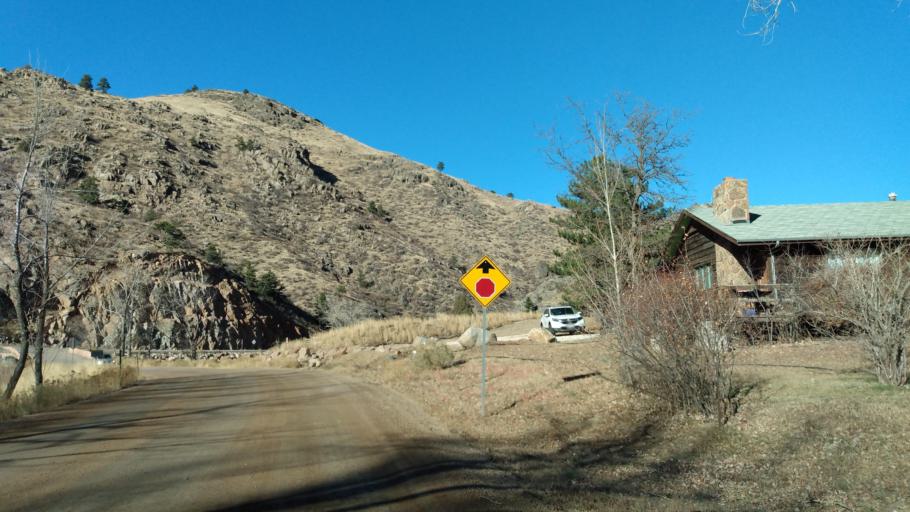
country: US
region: Colorado
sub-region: Boulder County
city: Lyons
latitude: 40.2421
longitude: -105.3126
